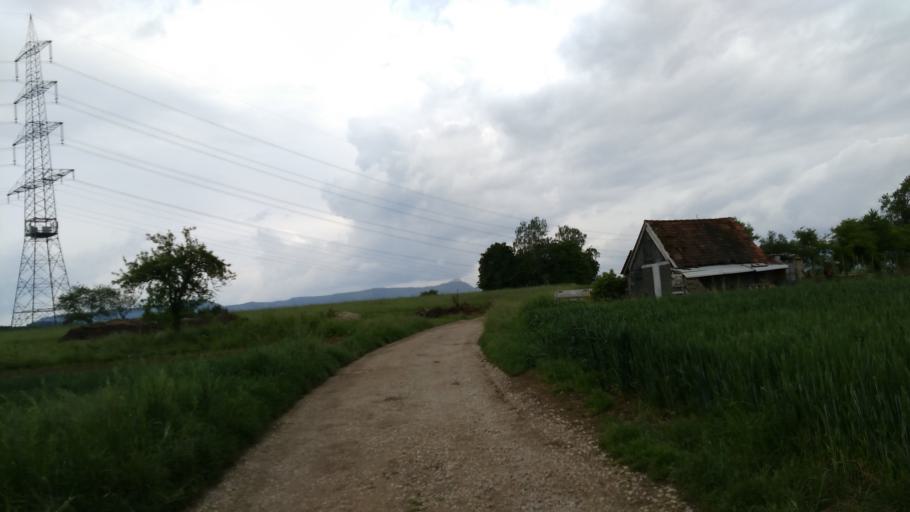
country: DE
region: Baden-Wuerttemberg
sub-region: Regierungsbezirk Stuttgart
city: Oberboihingen
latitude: 48.6282
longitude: 9.3738
